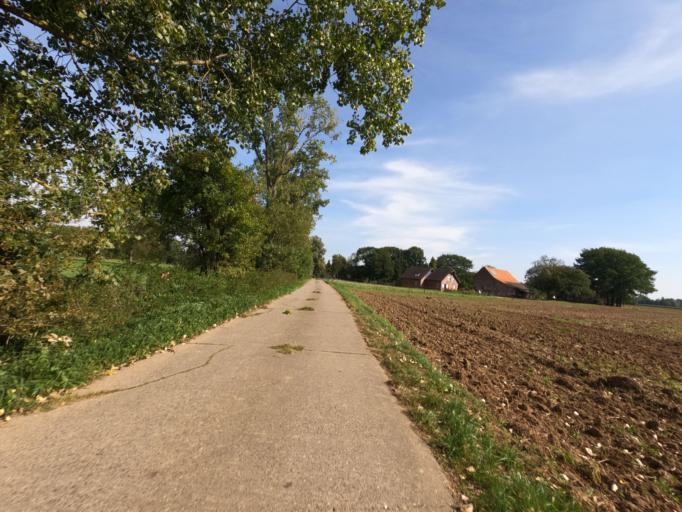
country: DE
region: North Rhine-Westphalia
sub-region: Regierungsbezirk Koln
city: Linnich
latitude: 50.9669
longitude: 6.2912
